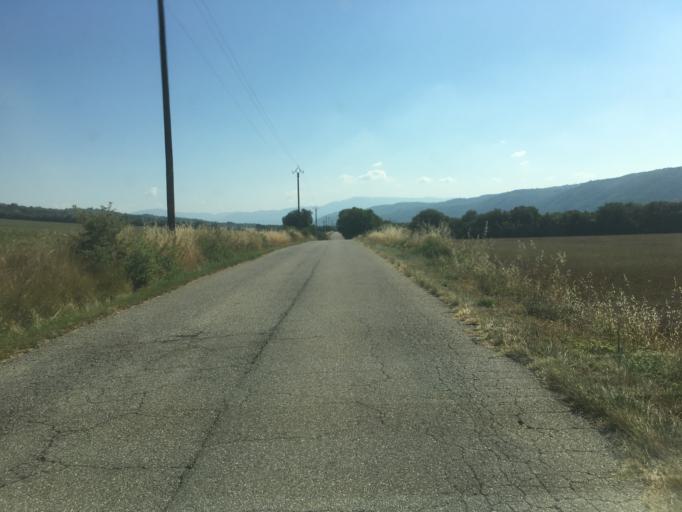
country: FR
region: Provence-Alpes-Cote d'Azur
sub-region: Departement des Alpes-de-Haute-Provence
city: Oraison
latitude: 43.8919
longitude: 5.9649
